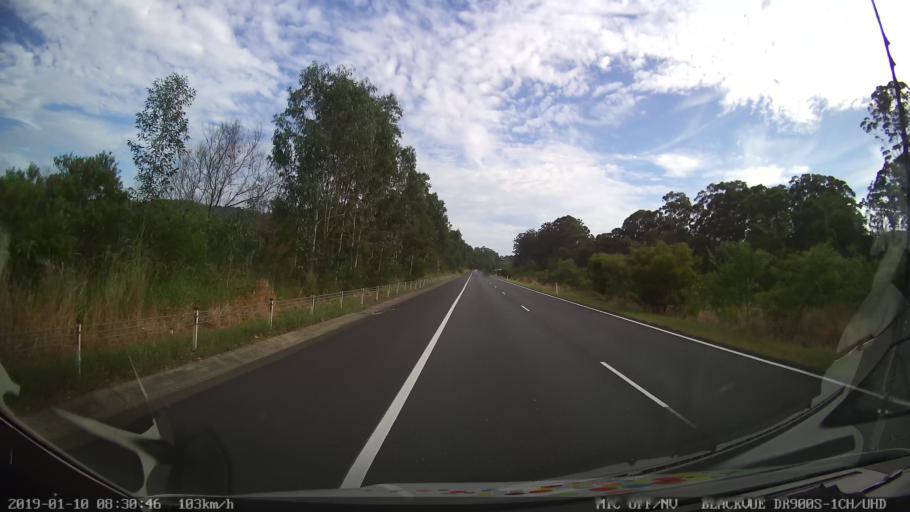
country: AU
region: New South Wales
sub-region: Coffs Harbour
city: Bonville
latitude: -30.3660
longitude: 153.0543
